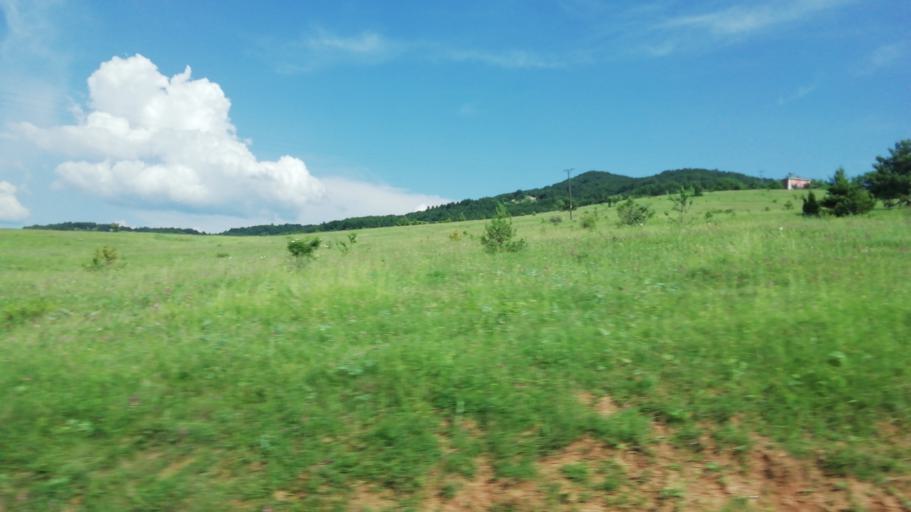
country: TR
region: Karabuk
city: Karabuk
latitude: 41.1287
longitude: 32.5760
